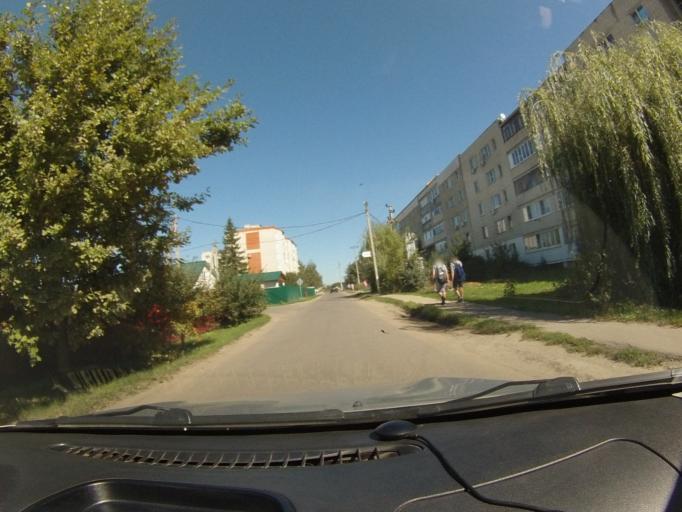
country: RU
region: Tambov
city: Donskoye
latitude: 52.7633
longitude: 41.4717
